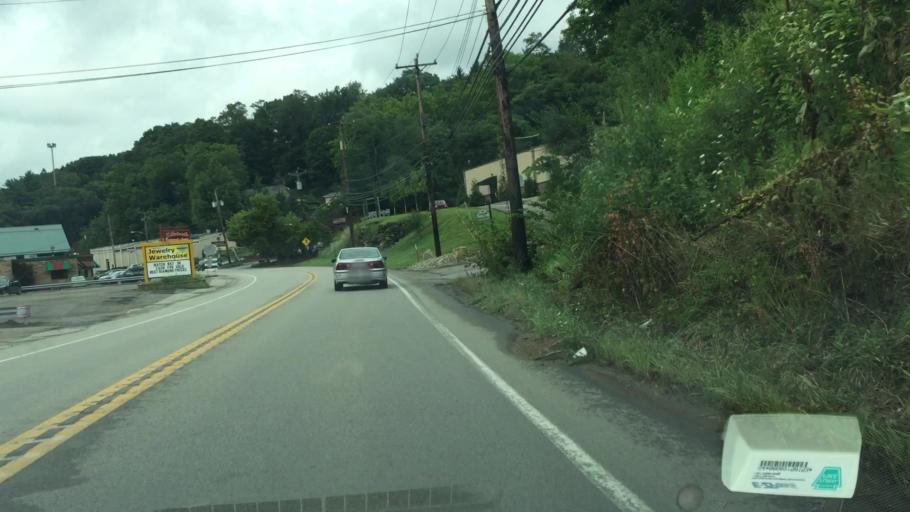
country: US
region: Pennsylvania
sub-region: Allegheny County
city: Millvale
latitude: 40.5085
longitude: -79.9905
